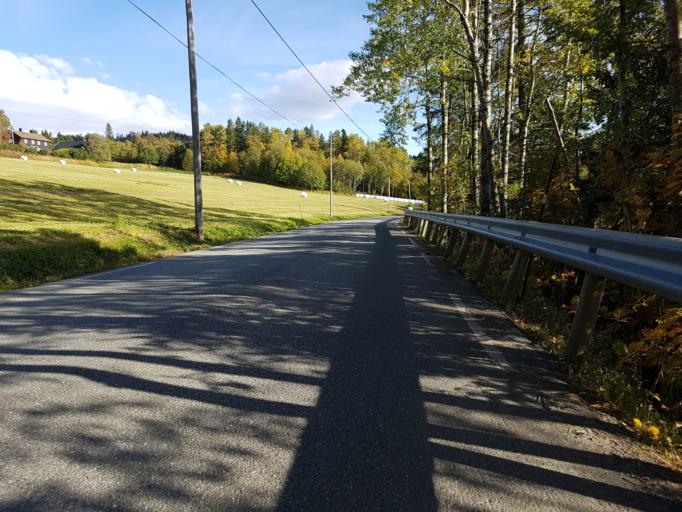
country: NO
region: Sor-Trondelag
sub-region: Malvik
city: Malvik
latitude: 63.3837
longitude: 10.5906
